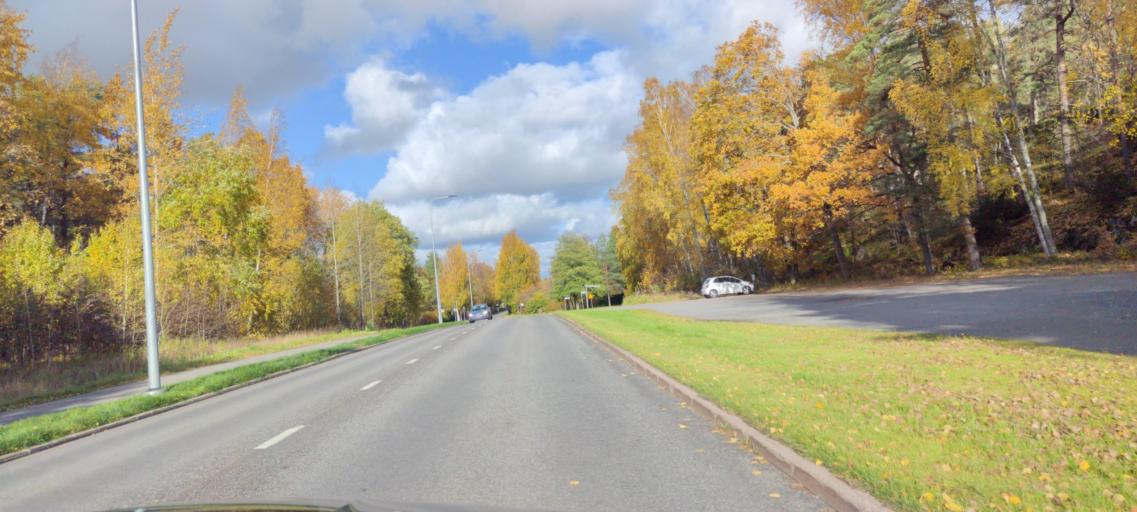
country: FI
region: Varsinais-Suomi
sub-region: Turku
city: Turku
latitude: 60.4170
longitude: 22.2693
